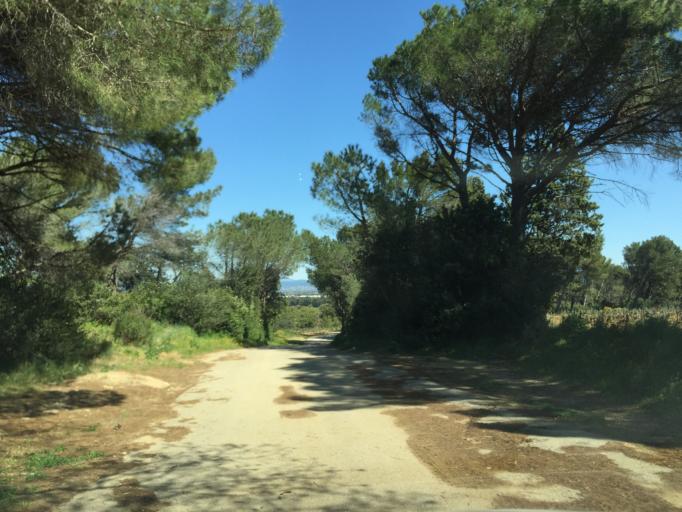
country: FR
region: Provence-Alpes-Cote d'Azur
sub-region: Departement du Vaucluse
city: Chateauneuf-du-Pape
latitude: 44.0801
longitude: 4.8459
